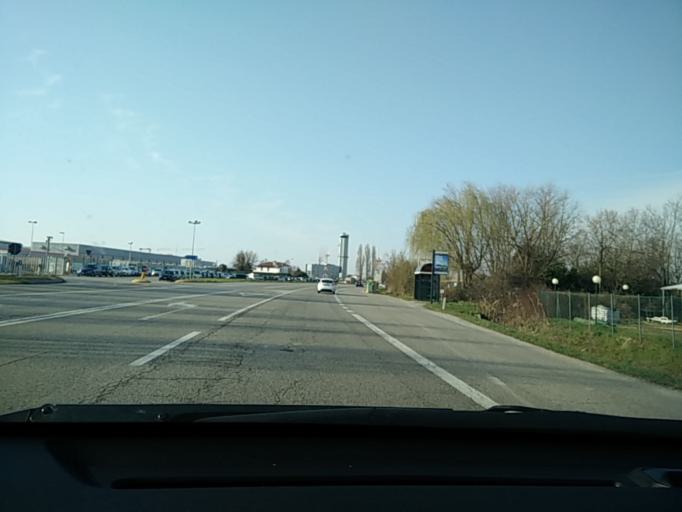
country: IT
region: Veneto
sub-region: Provincia di Venezia
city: Tessera
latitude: 45.5145
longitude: 12.3524
